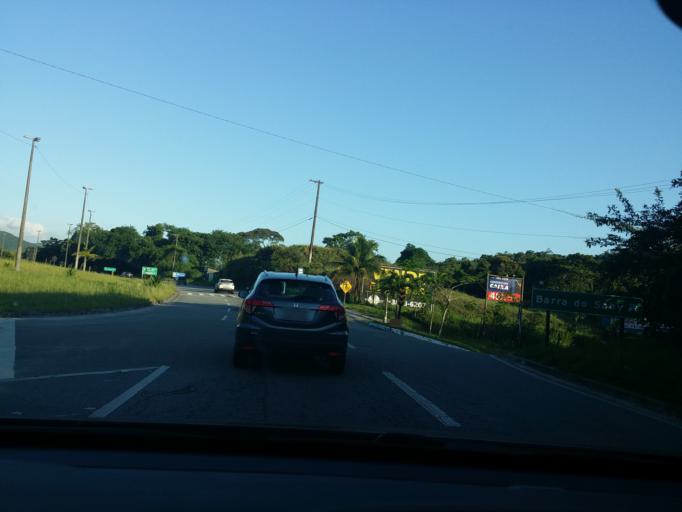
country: BR
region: Sao Paulo
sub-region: Sao Sebastiao
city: Sao Sebastiao
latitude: -23.7699
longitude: -45.6894
